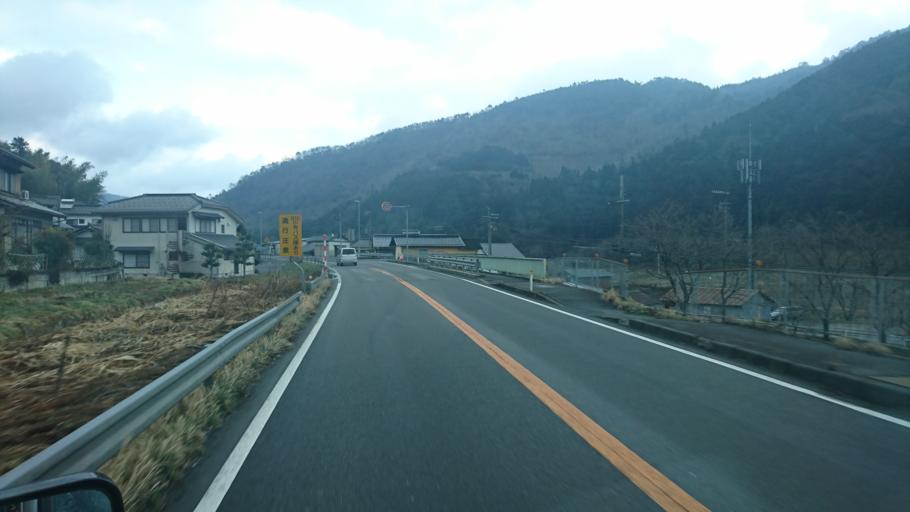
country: JP
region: Hyogo
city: Toyooka
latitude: 35.3808
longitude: 134.6658
